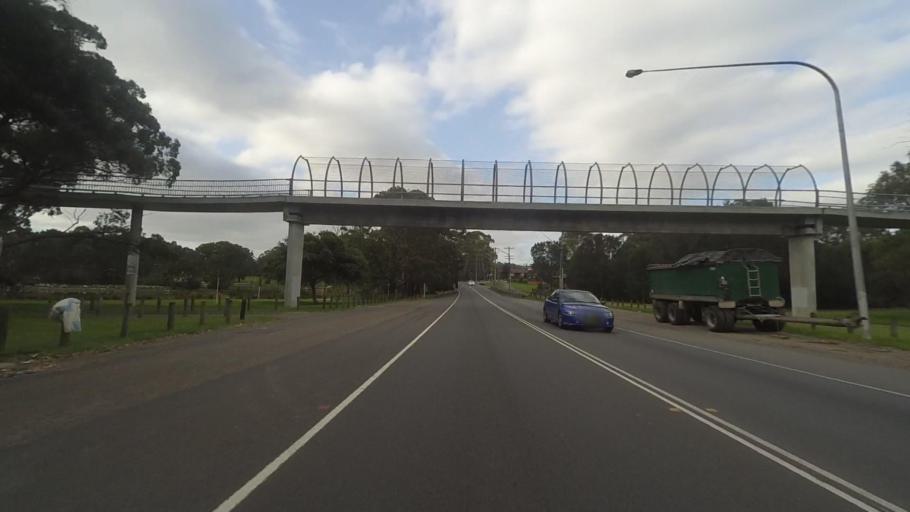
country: AU
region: New South Wales
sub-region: Bankstown
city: Milperra
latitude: -33.9083
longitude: 150.9818
